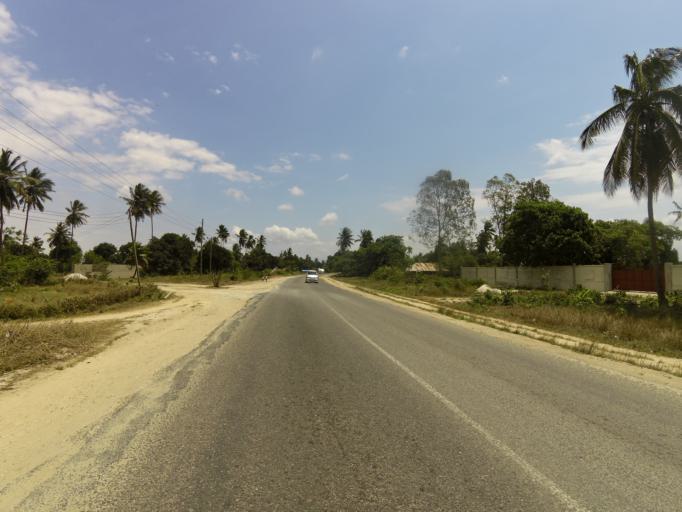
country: TZ
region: Pwani
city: Vikindu
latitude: -7.0320
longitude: 39.2914
